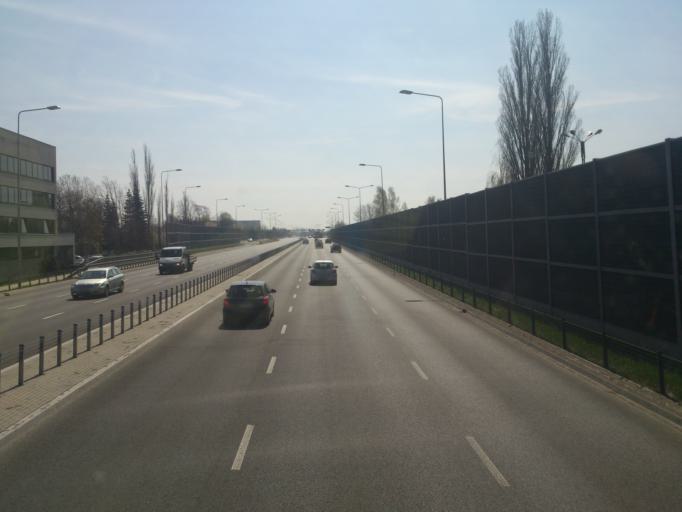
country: PL
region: Lodz Voivodeship
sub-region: Powiat lodzki wschodni
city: Starowa Gora
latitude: 51.7094
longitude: 19.4635
